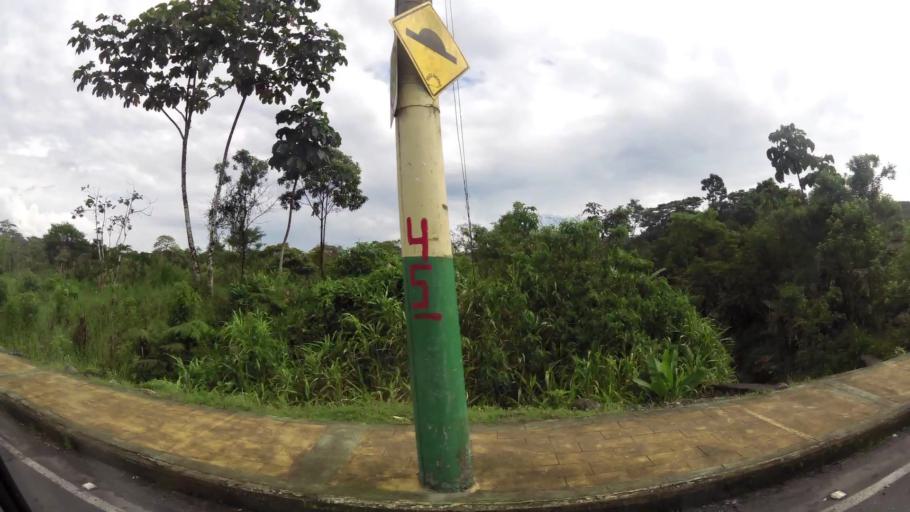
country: EC
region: Pastaza
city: Puyo
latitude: -1.4851
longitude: -77.9940
